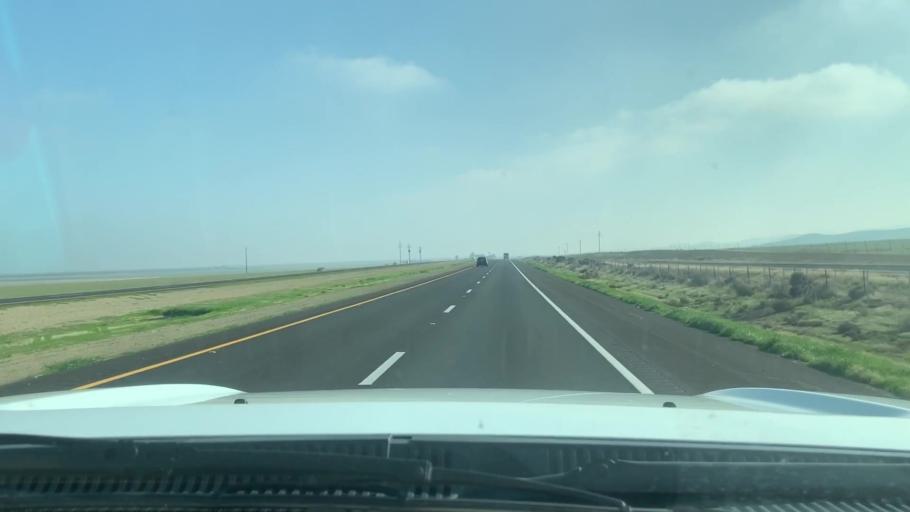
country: US
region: California
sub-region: San Luis Obispo County
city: Shandon
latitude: 35.6490
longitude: -120.0363
